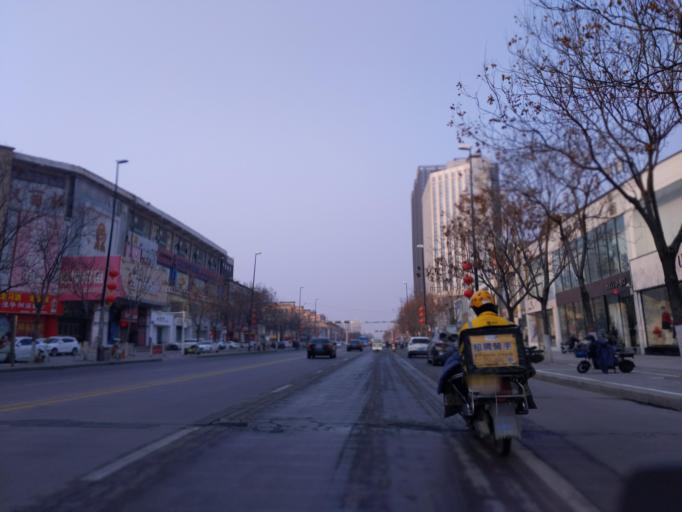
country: CN
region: Henan Sheng
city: Zhongyuanlu
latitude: 35.7687
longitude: 115.0584
